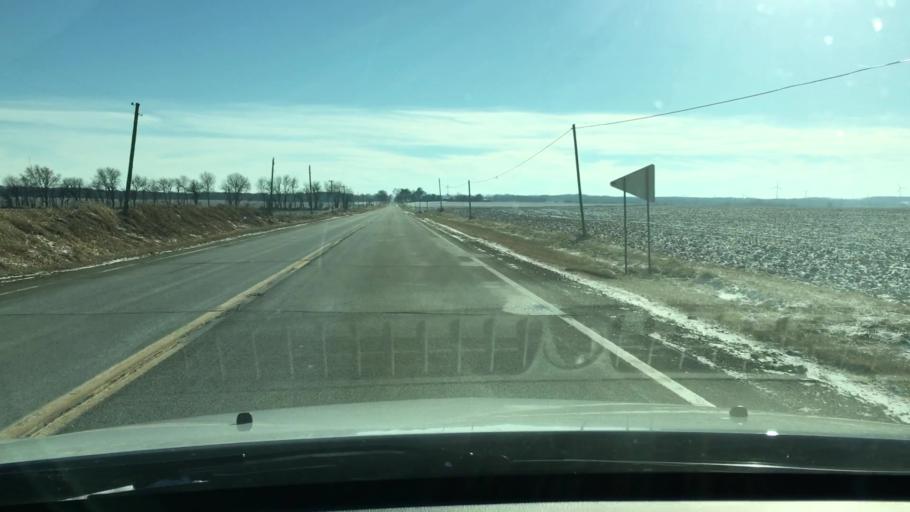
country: US
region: Illinois
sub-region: Ogle County
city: Rochelle
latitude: 41.7519
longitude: -89.0842
